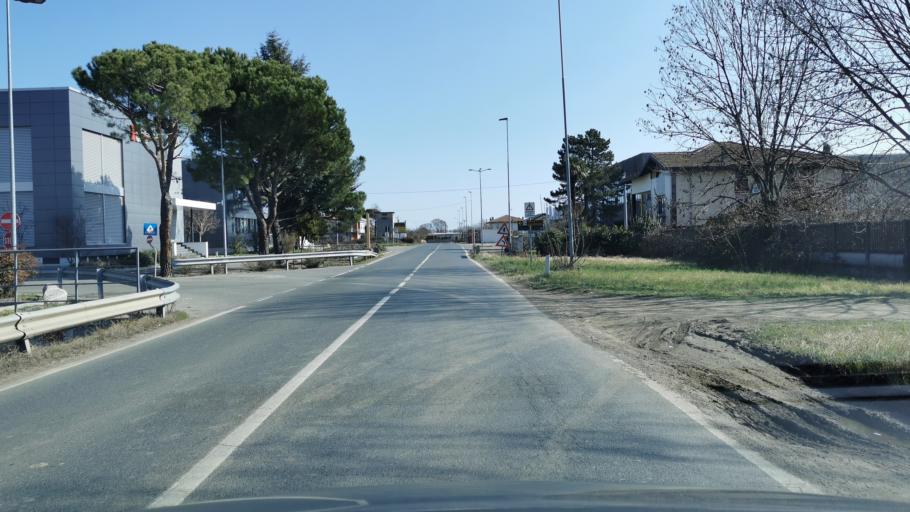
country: IT
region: Piedmont
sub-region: Provincia di Torino
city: Busano
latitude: 45.3290
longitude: 7.6681
